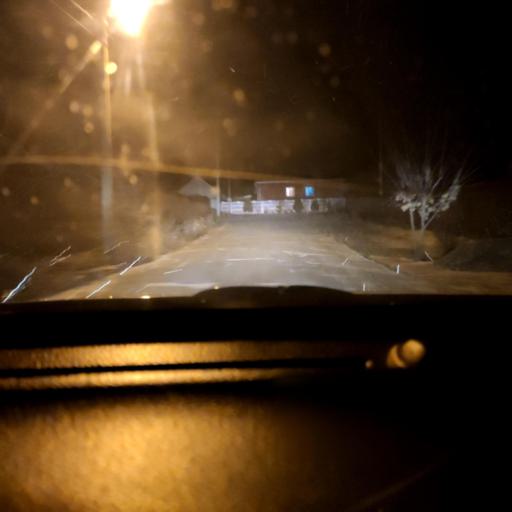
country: RU
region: Voronezj
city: Maslovka
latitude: 51.5780
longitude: 39.3244
